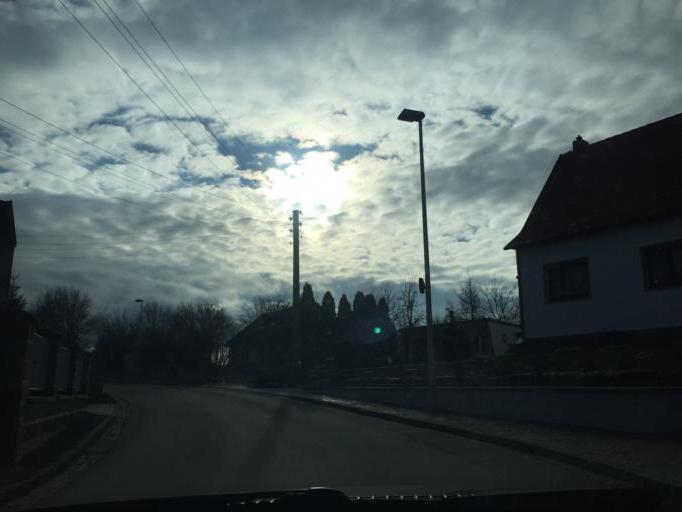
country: DE
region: Saxony
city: Ebersbach
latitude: 51.2300
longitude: 13.6617
